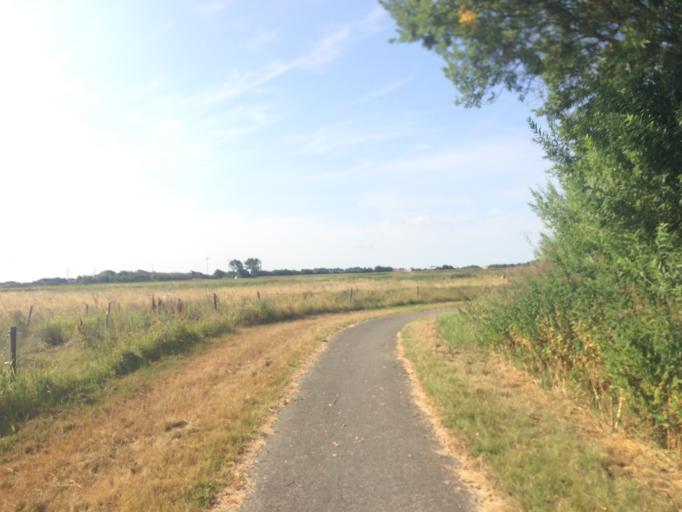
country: DK
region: Central Jutland
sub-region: Holstebro Kommune
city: Vinderup
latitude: 56.6165
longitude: 8.7769
